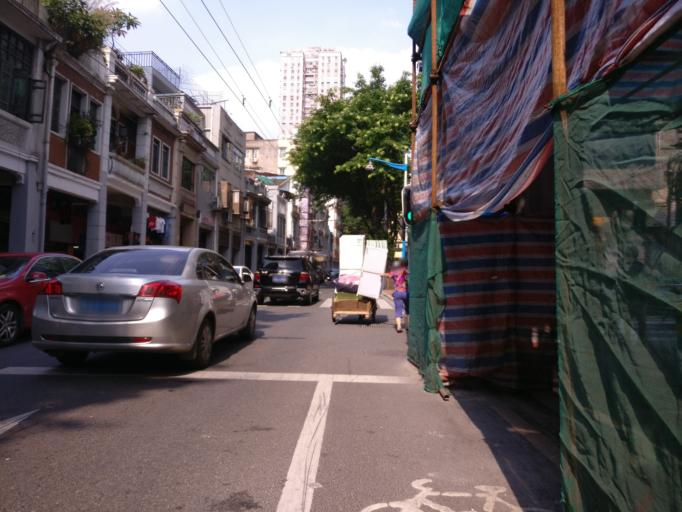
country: CN
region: Guangdong
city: Guangzhou
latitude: 23.1248
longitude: 113.2756
